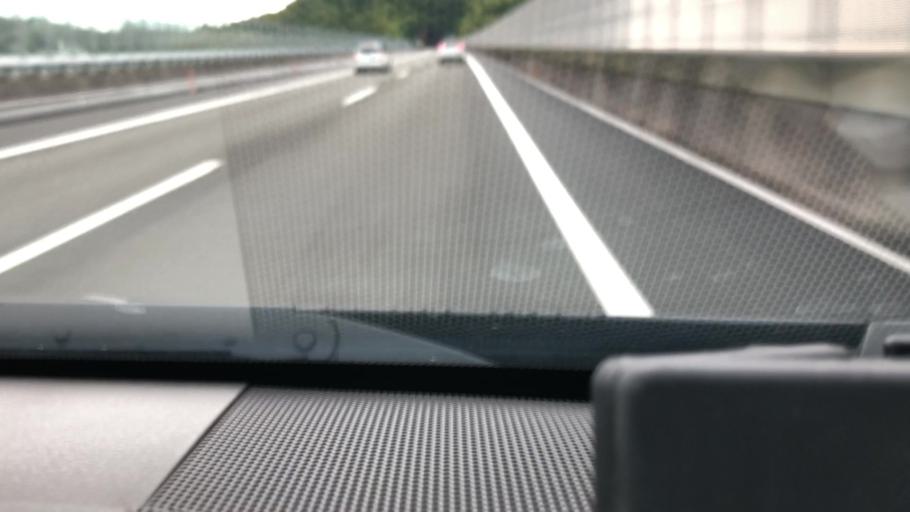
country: JP
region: Shizuoka
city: Fujieda
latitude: 34.8862
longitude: 138.2131
